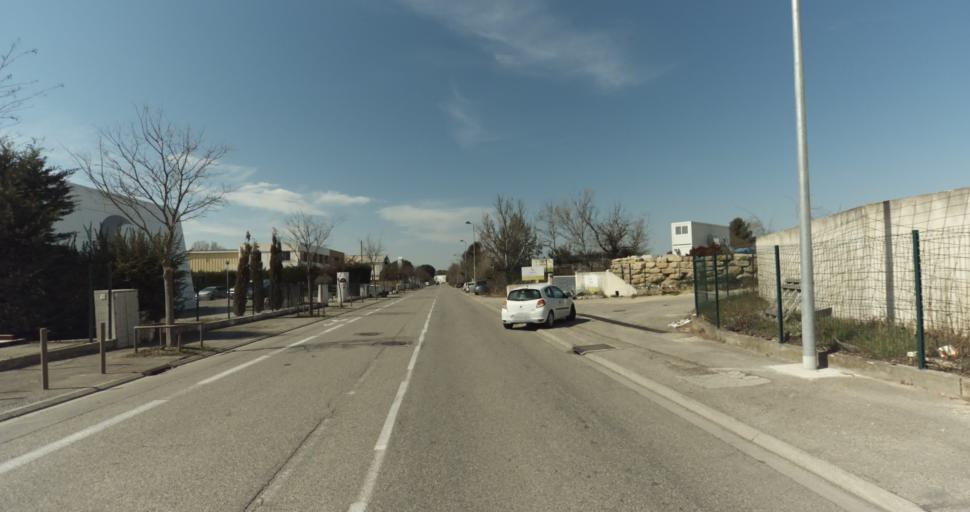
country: FR
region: Provence-Alpes-Cote d'Azur
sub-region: Departement des Bouches-du-Rhone
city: Cabries
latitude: 43.4826
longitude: 5.3776
